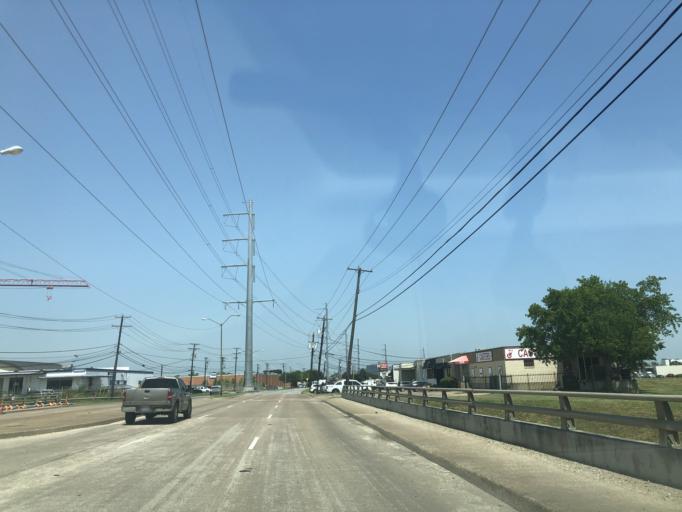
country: US
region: Texas
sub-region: Dallas County
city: Dallas
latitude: 32.7964
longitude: -96.8355
